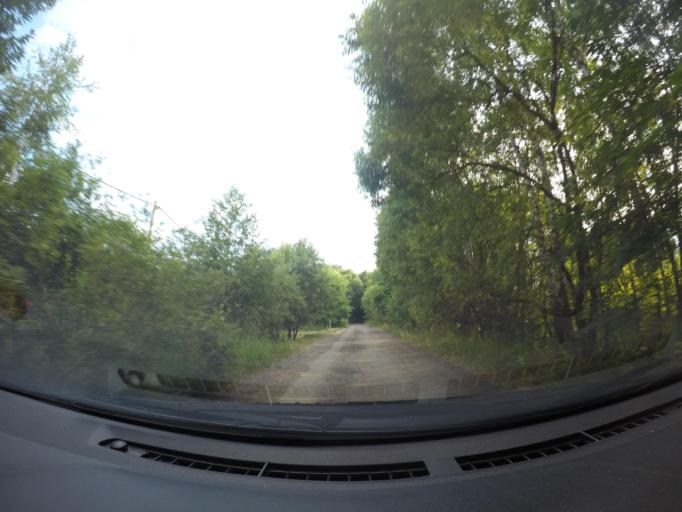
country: RU
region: Moskovskaya
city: Krasnyy Tkach
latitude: 55.4200
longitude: 39.2359
